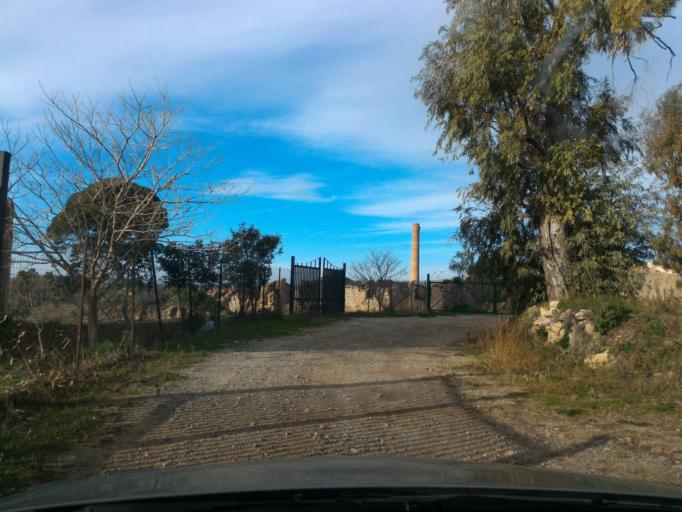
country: IT
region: Calabria
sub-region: Provincia di Crotone
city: Isola di Capo Rizzuto
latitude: 38.9868
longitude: 17.0639
